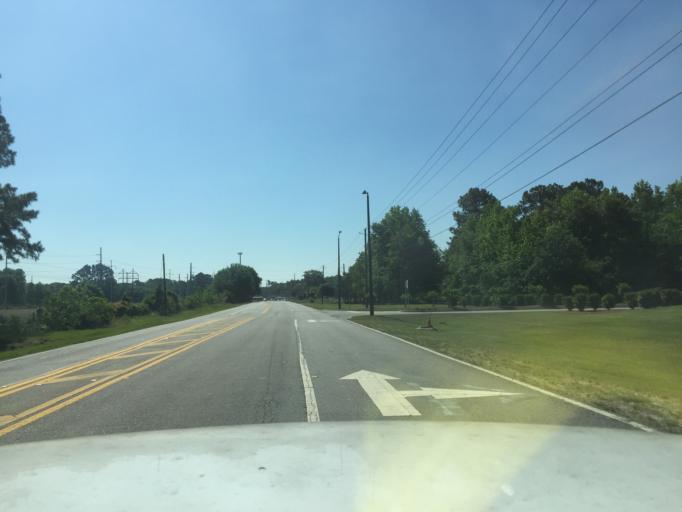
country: US
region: Georgia
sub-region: Chatham County
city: Georgetown
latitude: 32.0054
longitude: -81.2493
